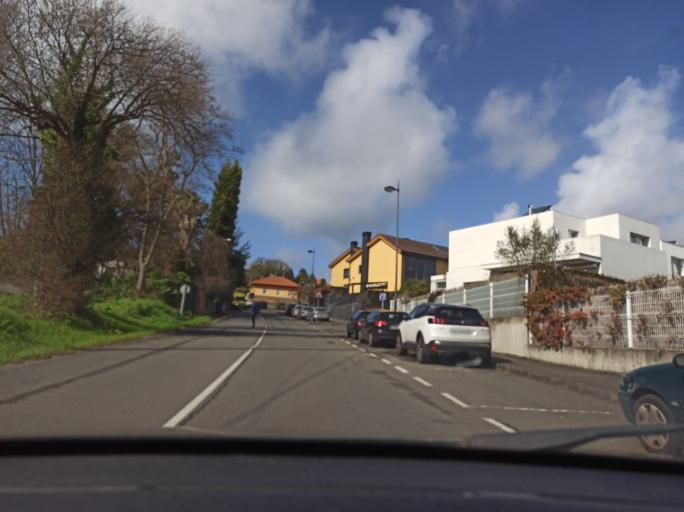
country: ES
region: Galicia
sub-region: Provincia da Coruna
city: Cambre
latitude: 43.3231
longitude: -8.3527
